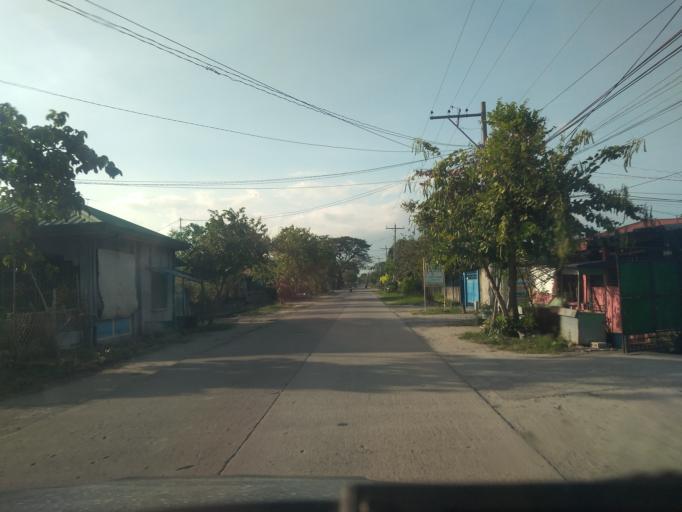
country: PH
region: Central Luzon
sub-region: Province of Pampanga
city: Bulaon
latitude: 15.0922
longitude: 120.6857
